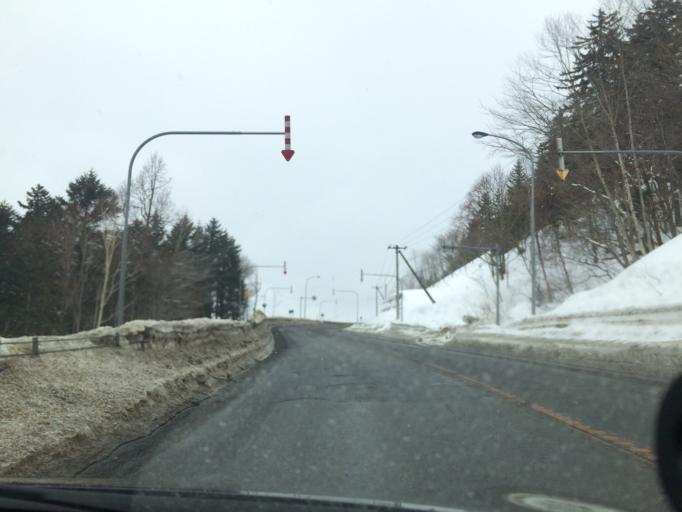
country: JP
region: Hokkaido
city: Shimo-furano
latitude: 42.8898
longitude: 142.2987
